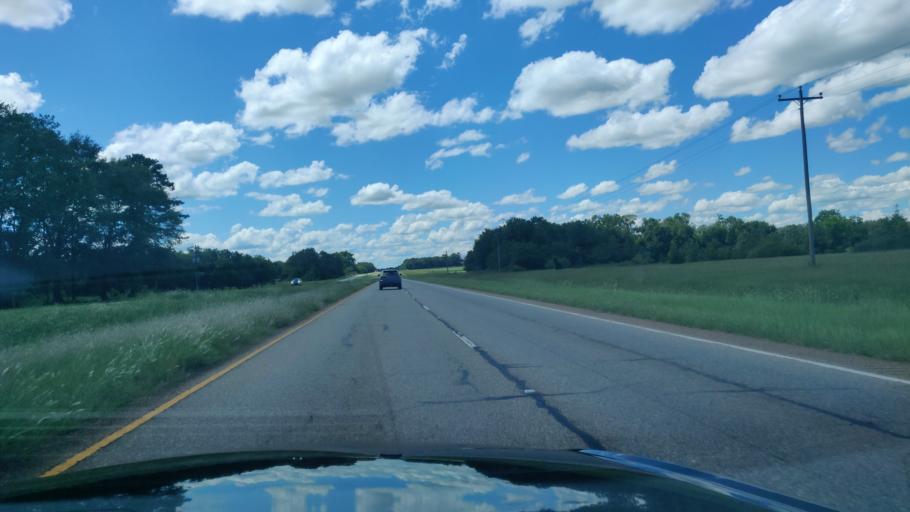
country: US
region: Georgia
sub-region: Webster County
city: Preston
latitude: 31.9513
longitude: -84.5808
